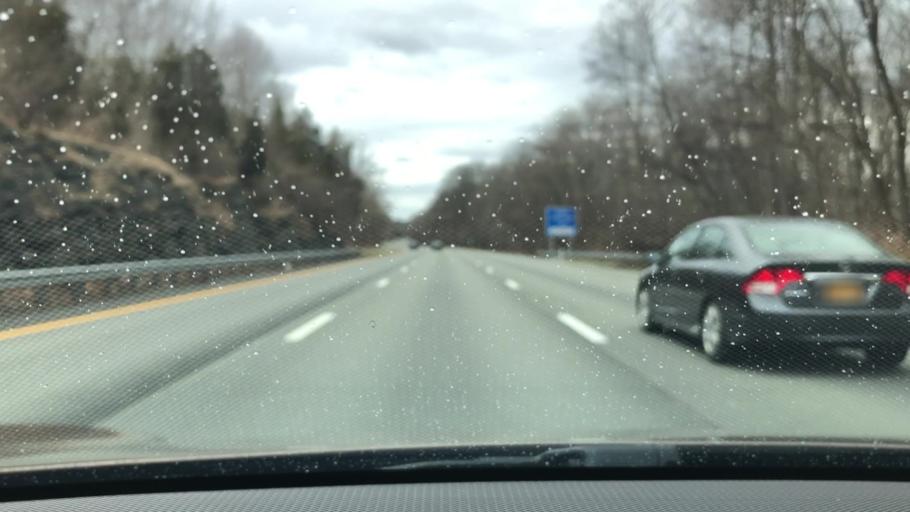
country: US
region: New Jersey
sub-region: Warren County
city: Belvidere
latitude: 40.9281
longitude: -75.0415
